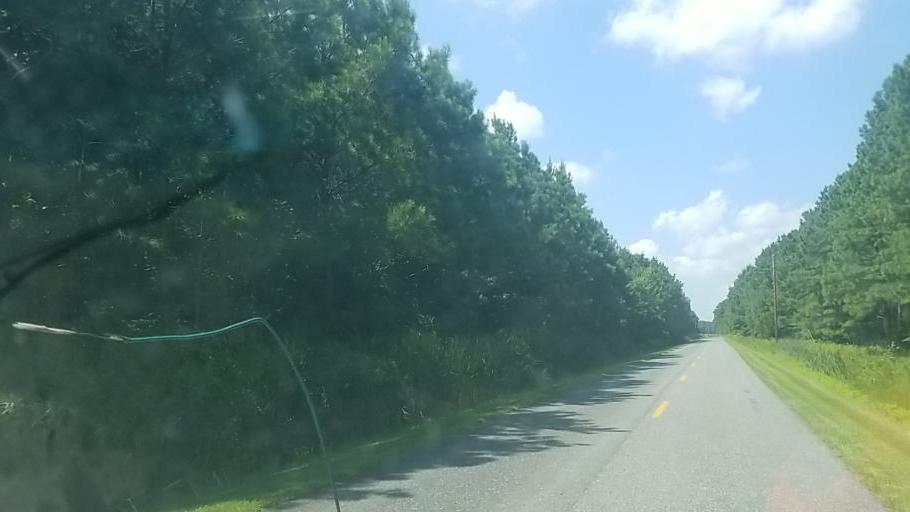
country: US
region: Maryland
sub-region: Wicomico County
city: Hebron
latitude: 38.4411
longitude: -75.8452
